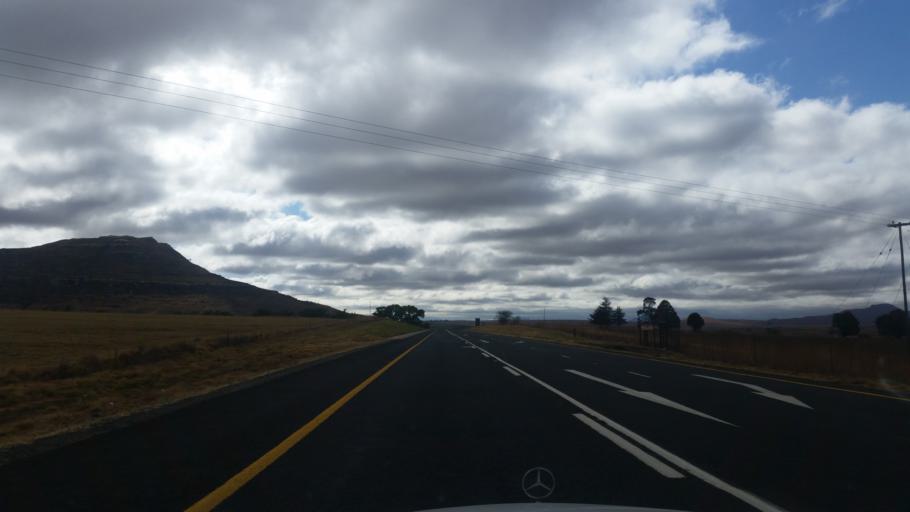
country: ZA
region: Orange Free State
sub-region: Thabo Mofutsanyana District Municipality
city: Phuthaditjhaba
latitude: -28.3129
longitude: 28.7391
